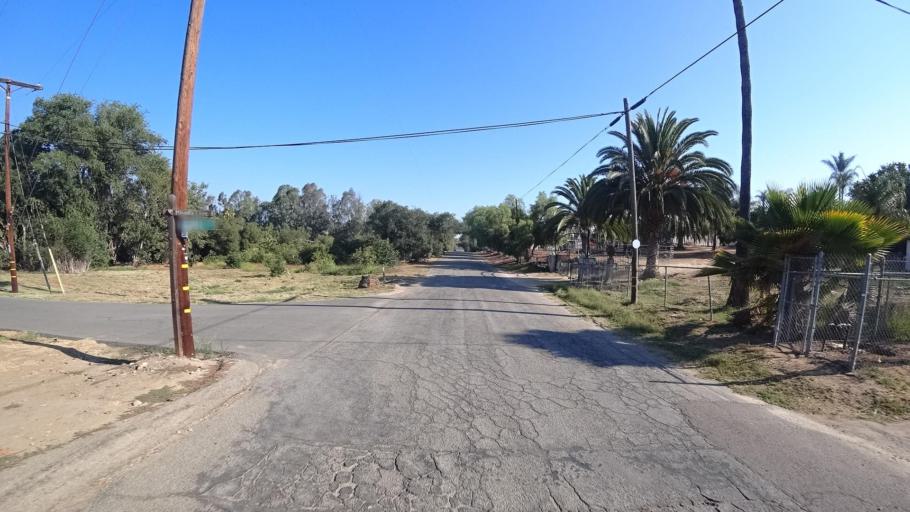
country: US
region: California
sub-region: San Diego County
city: Fallbrook
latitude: 33.3266
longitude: -117.2601
